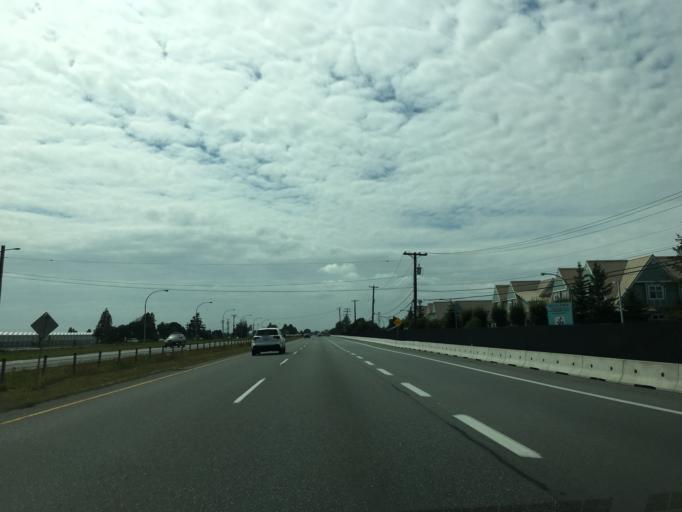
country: CA
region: British Columbia
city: Delta
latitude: 49.0906
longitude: -122.9626
